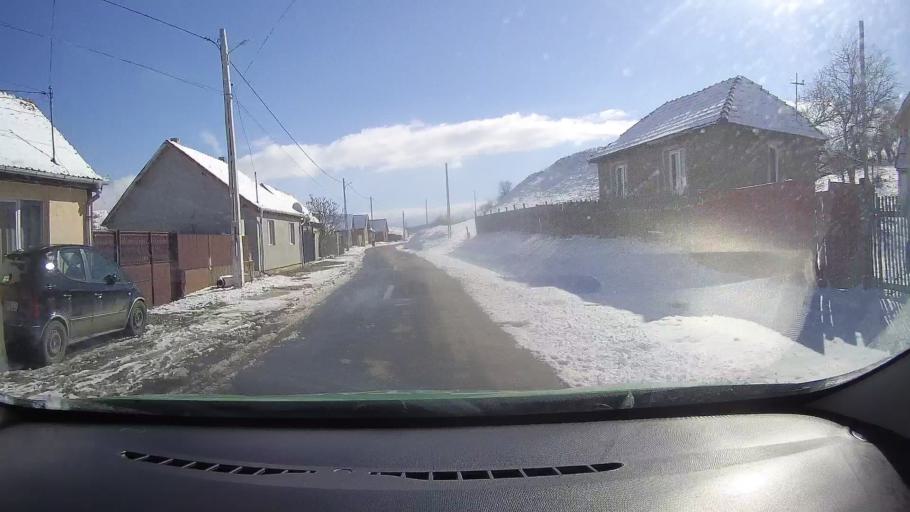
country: RO
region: Sibiu
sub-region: Comuna Rosia
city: Rosia
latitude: 45.7984
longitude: 24.2904
